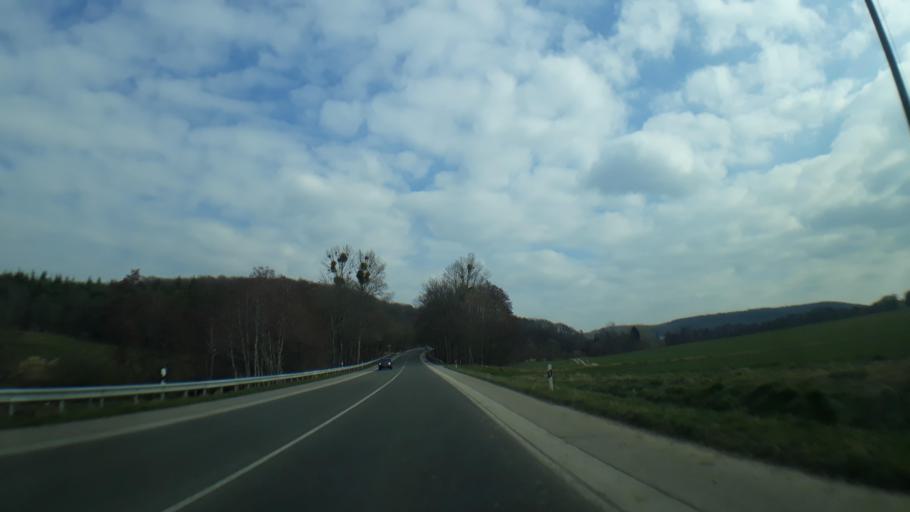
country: DE
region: North Rhine-Westphalia
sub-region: Regierungsbezirk Koln
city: Rheinbach
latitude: 50.5998
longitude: 6.8775
